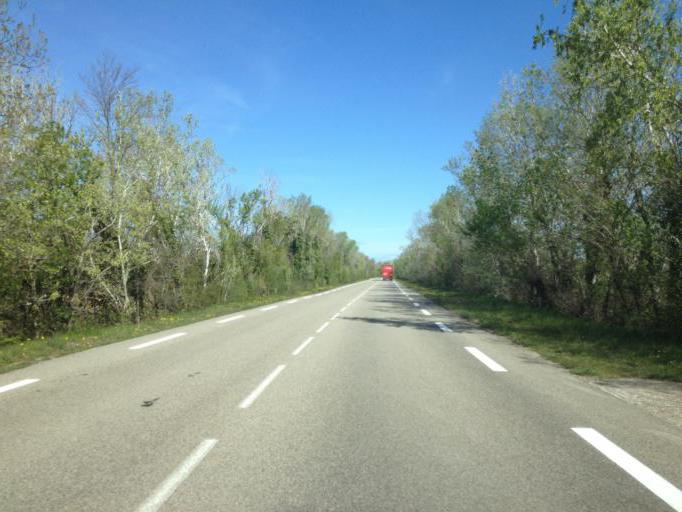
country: FR
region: Provence-Alpes-Cote d'Azur
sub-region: Departement du Vaucluse
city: Caderousse
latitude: 44.1201
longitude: 4.7197
